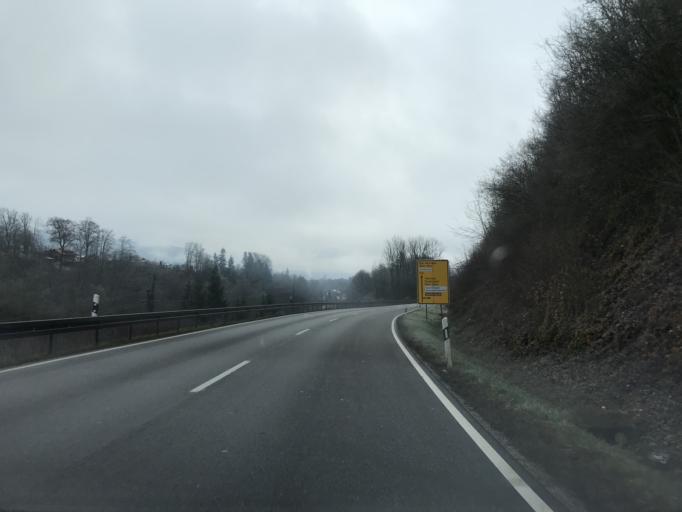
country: DE
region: Baden-Wuerttemberg
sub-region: Freiburg Region
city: Wehr
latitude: 47.6392
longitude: 7.8948
